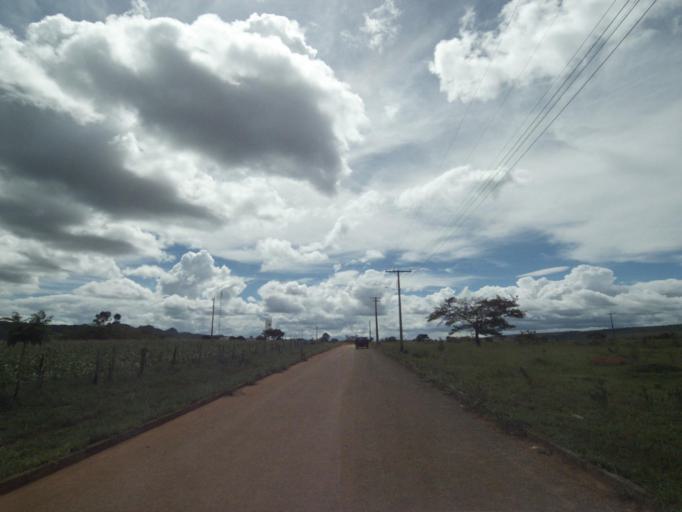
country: BR
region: Goias
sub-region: Pirenopolis
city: Pirenopolis
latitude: -15.7825
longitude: -48.7974
